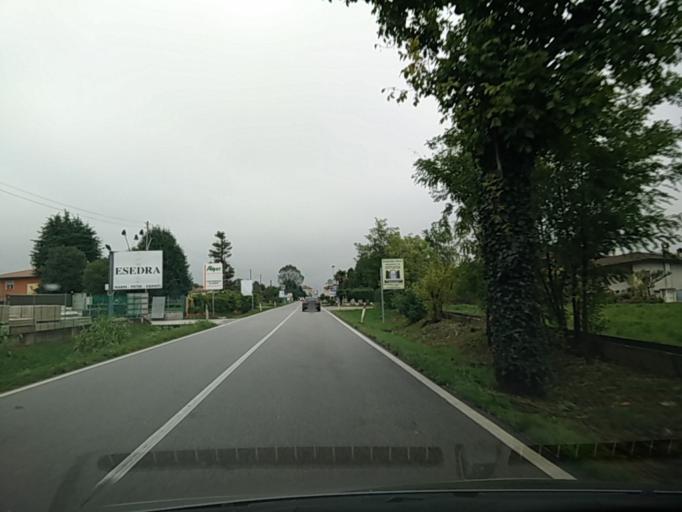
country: IT
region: Veneto
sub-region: Provincia di Treviso
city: Fossalunga
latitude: 45.6848
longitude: 12.0532
